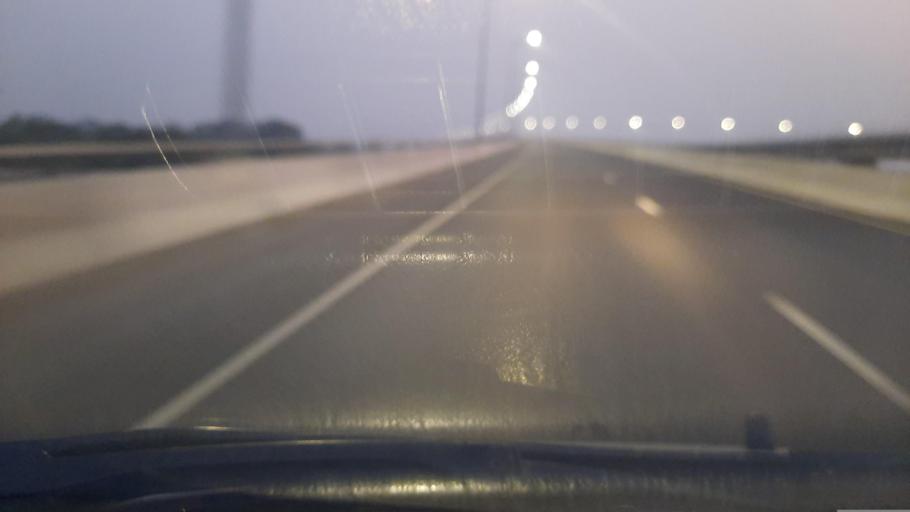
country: BD
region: Dhaka
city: Char Bhadrasan
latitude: 23.4093
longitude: 90.2555
